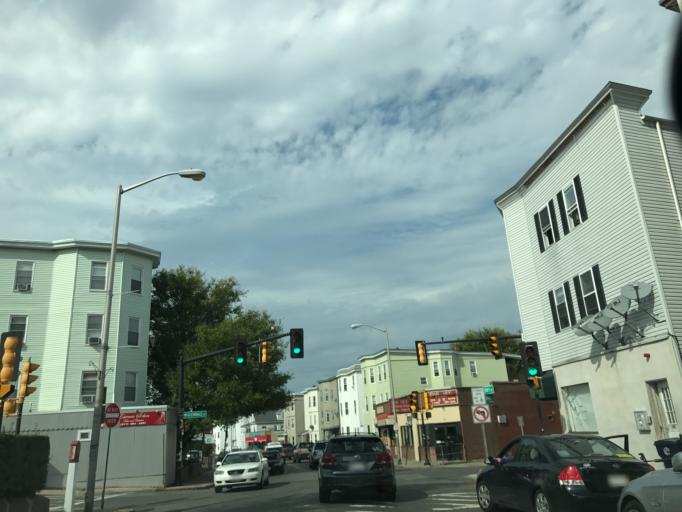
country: US
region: Massachusetts
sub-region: Middlesex County
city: Everett
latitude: 42.4169
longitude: -71.0492
